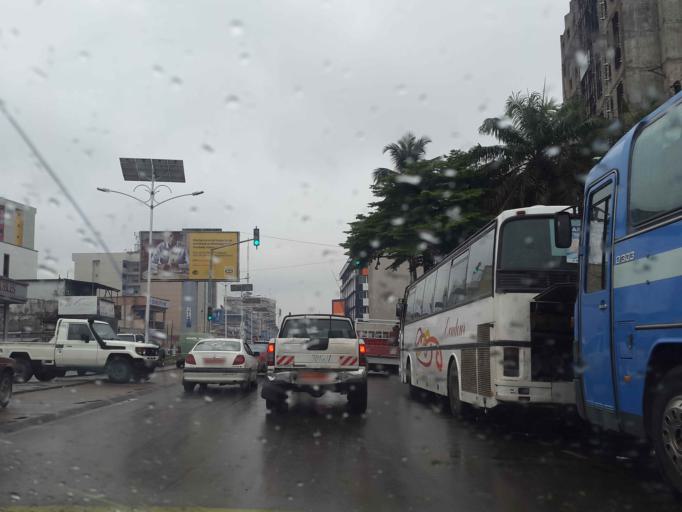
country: CM
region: Littoral
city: Douala
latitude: 4.0571
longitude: 9.6998
